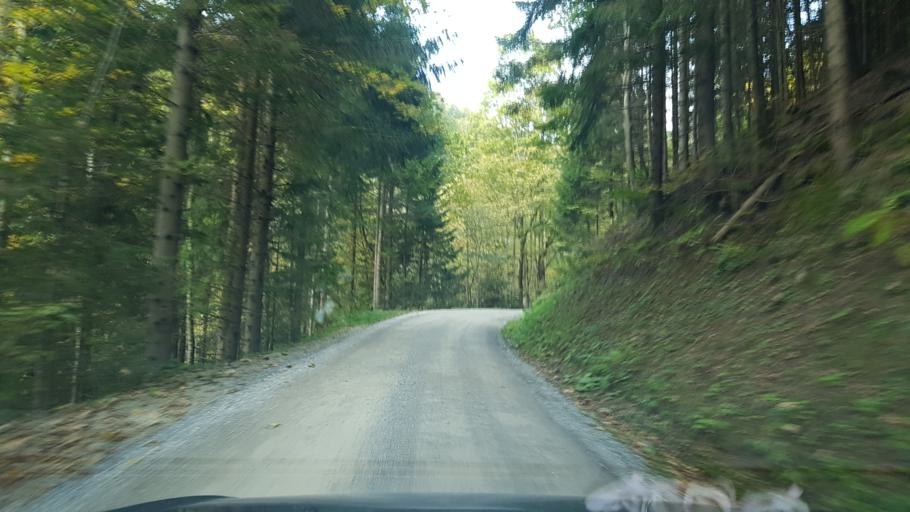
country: SI
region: Slovenj Gradec
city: Legen
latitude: 46.5173
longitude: 15.1290
